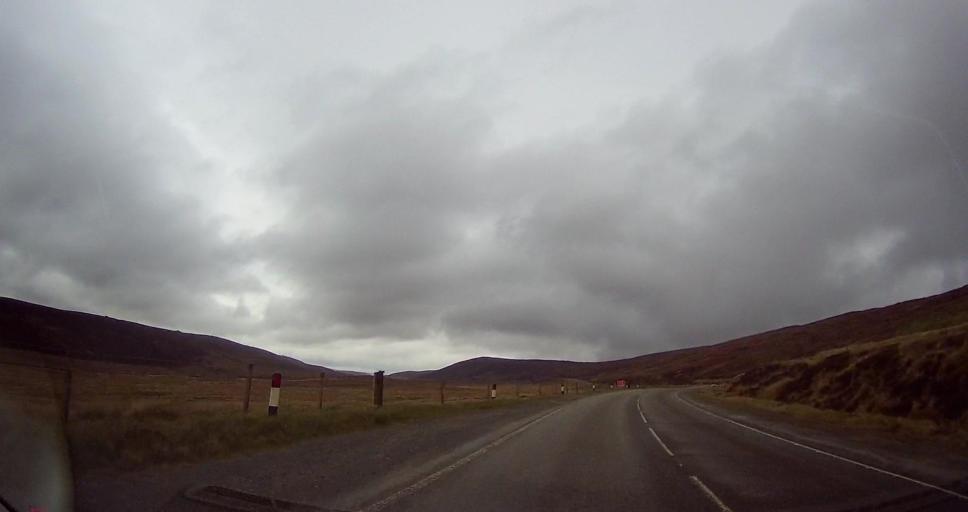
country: GB
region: Scotland
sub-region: Shetland Islands
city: Lerwick
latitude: 60.2834
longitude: -1.2438
